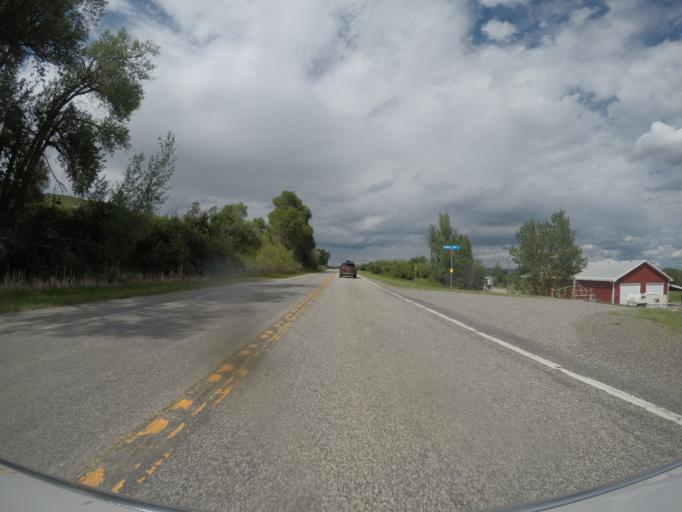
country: US
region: Montana
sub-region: Sweet Grass County
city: Big Timber
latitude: 45.8125
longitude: -109.9590
